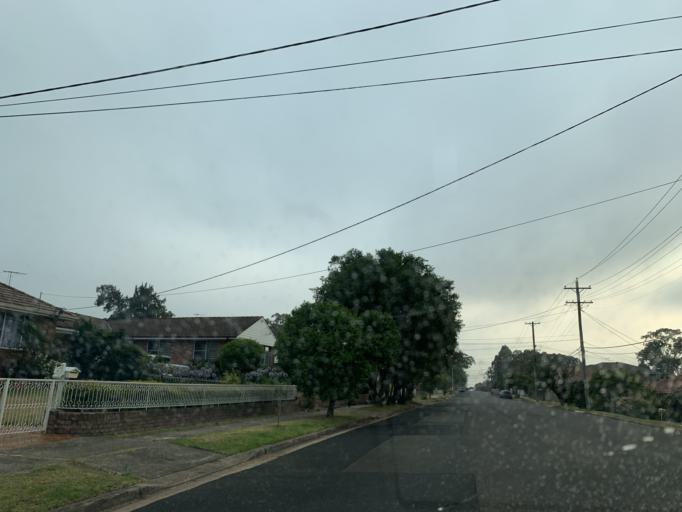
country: AU
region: New South Wales
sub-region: Parramatta
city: Carlingford
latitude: -33.7778
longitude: 151.0614
